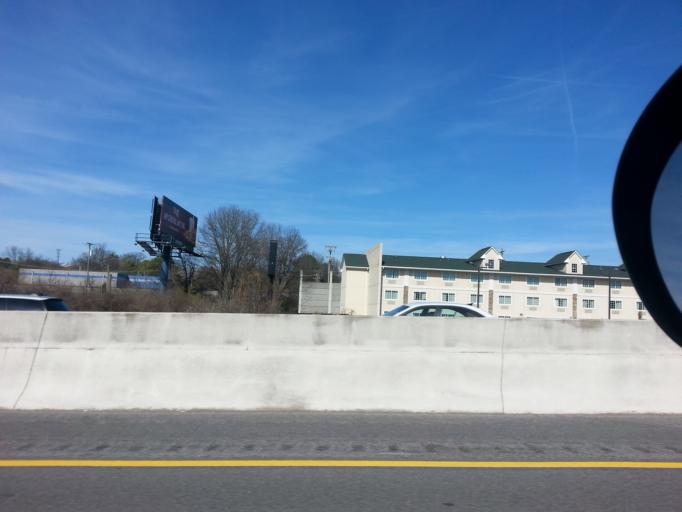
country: US
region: Tennessee
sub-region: Rutherford County
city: La Vergne
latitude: 36.0470
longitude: -86.6620
